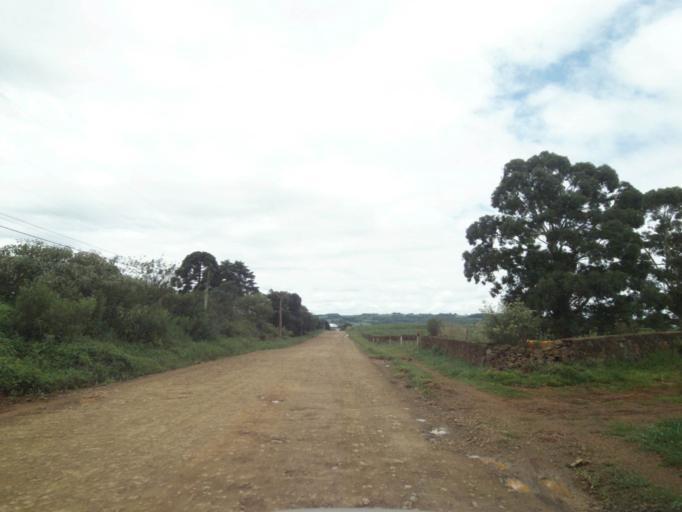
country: BR
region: Rio Grande do Sul
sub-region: Lagoa Vermelha
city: Lagoa Vermelha
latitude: -28.2203
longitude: -51.5374
